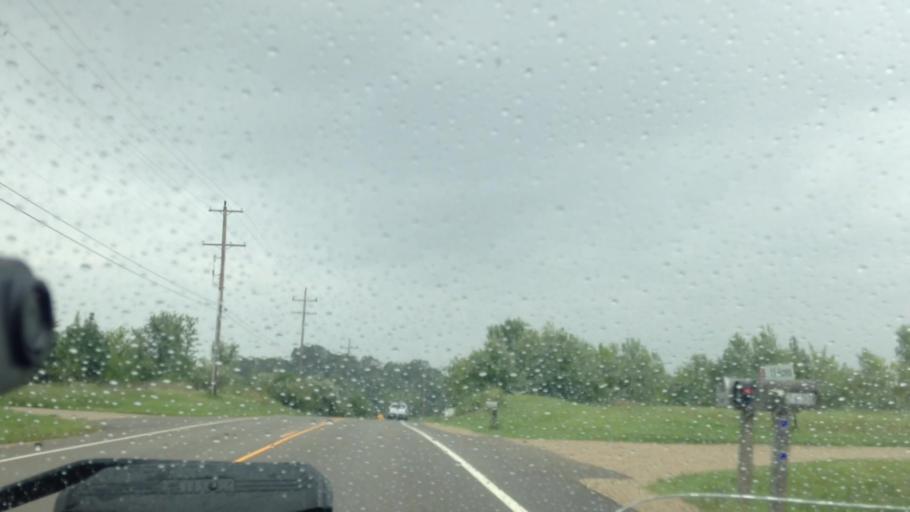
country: US
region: Wisconsin
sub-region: Washington County
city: Richfield
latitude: 43.2846
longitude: -88.2138
